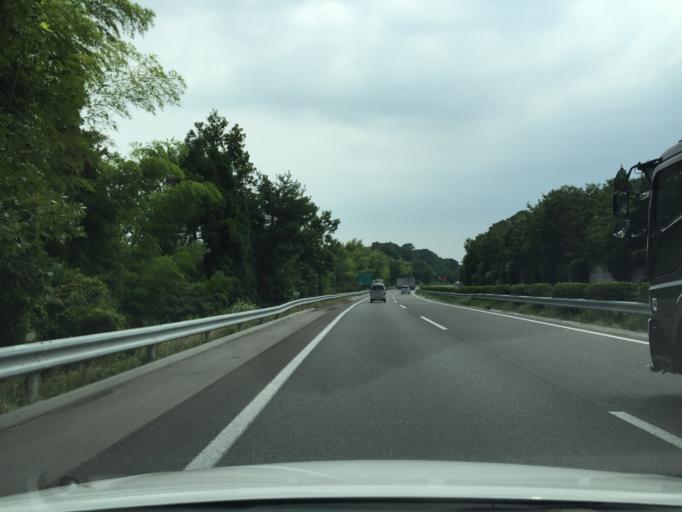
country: JP
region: Fukushima
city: Iwaki
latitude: 37.0115
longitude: 140.8143
